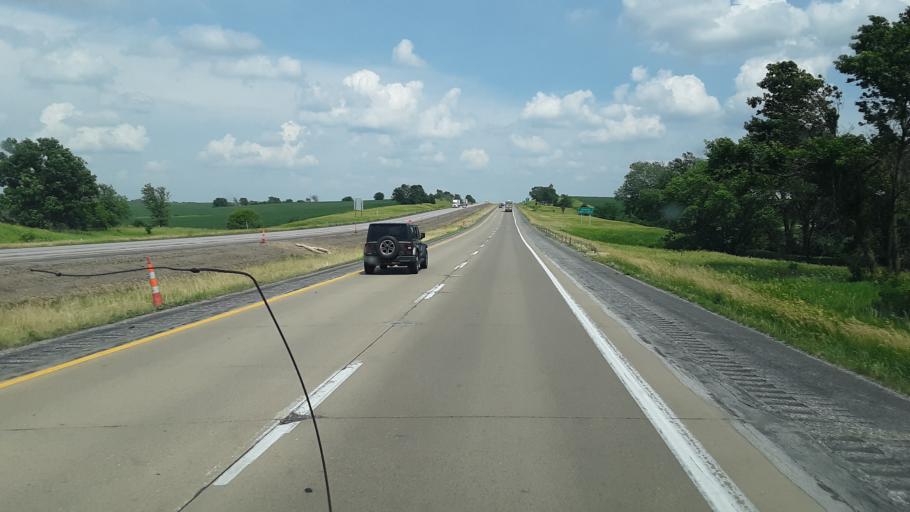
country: US
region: Iowa
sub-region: Cass County
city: Atlantic
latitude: 41.4981
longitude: -95.0937
